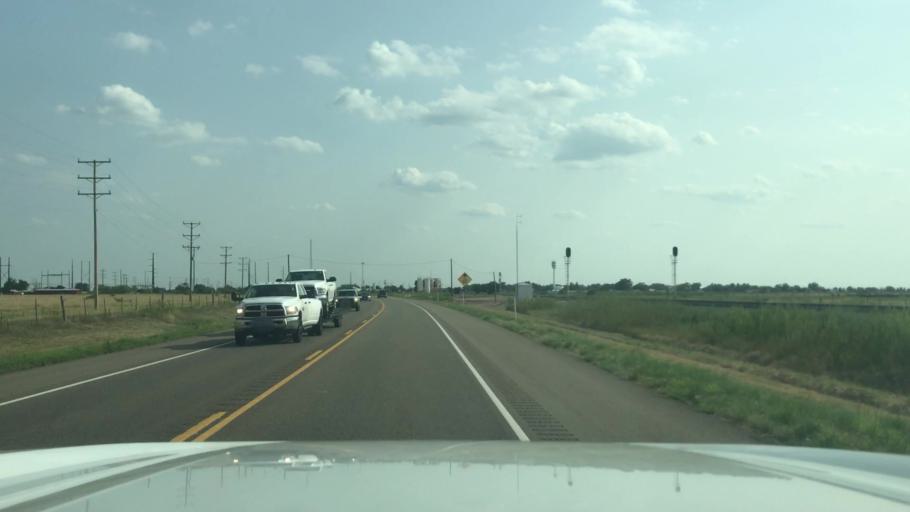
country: US
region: Texas
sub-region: Hartley County
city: Channing
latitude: 35.6962
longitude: -102.3278
